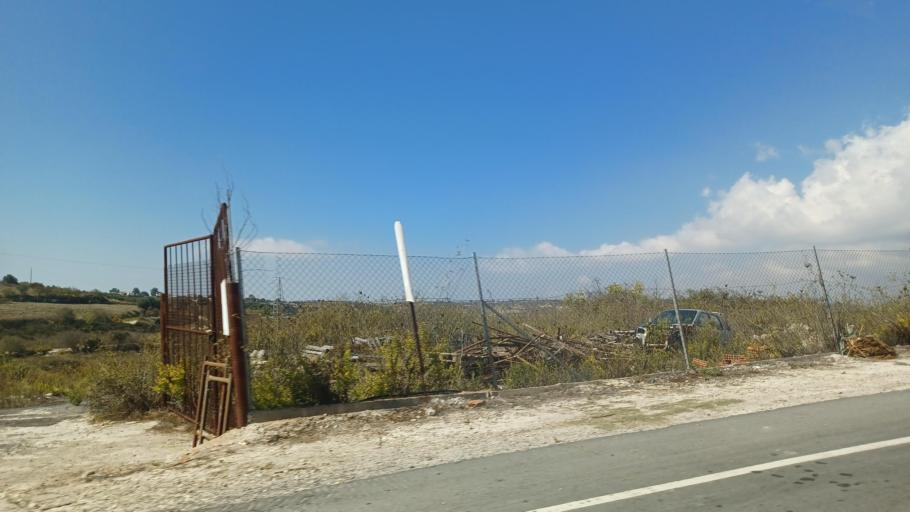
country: CY
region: Pafos
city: Mesogi
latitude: 34.8399
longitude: 32.4884
